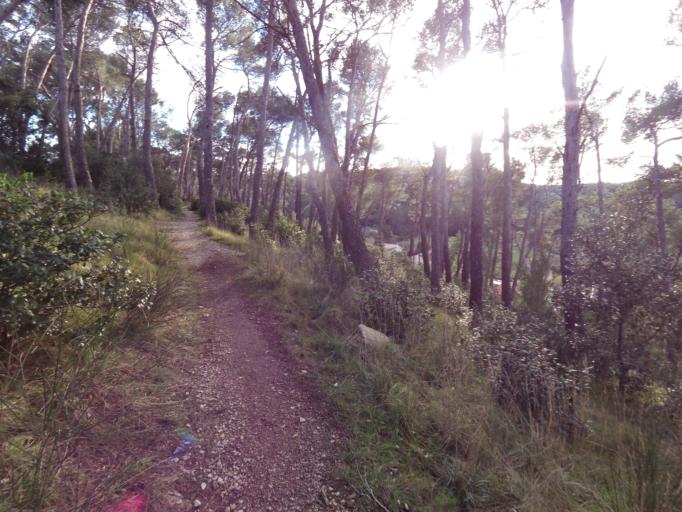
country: FR
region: Languedoc-Roussillon
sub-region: Departement du Gard
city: Langlade
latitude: 43.8025
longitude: 4.2495
